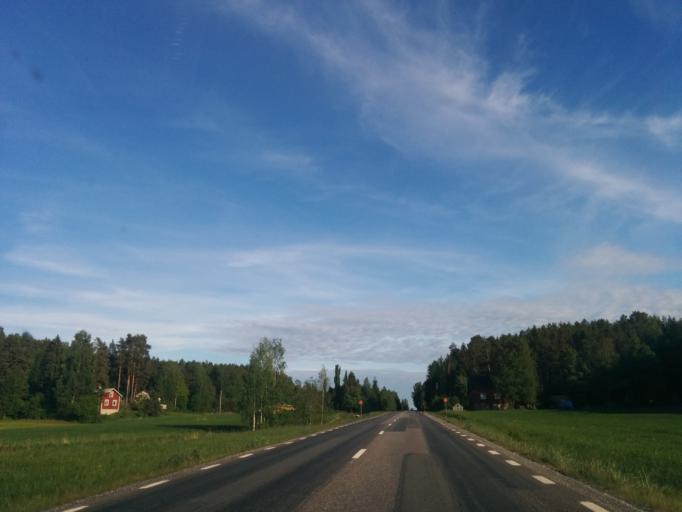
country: SE
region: Vaesternorrland
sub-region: Kramfors Kommun
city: Kramfors
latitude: 63.0178
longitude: 17.8244
